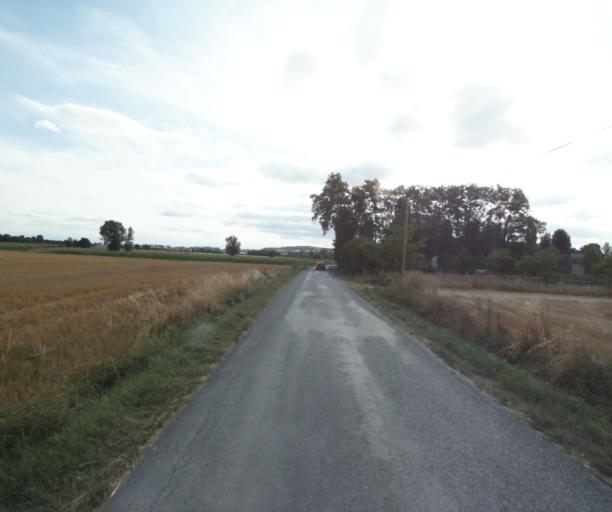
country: FR
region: Midi-Pyrenees
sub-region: Departement du Tarn
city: Puylaurens
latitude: 43.5216
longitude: 1.9686
